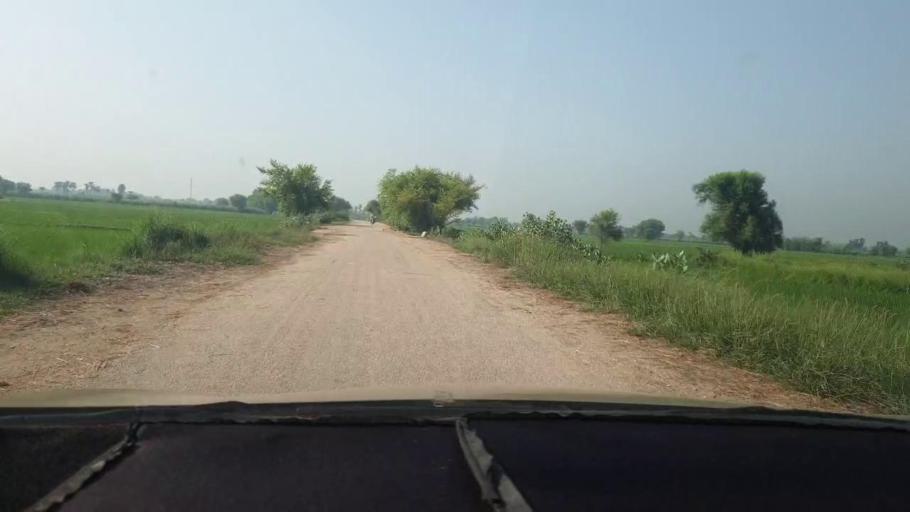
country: PK
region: Sindh
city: Kambar
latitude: 27.6190
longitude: 68.0904
